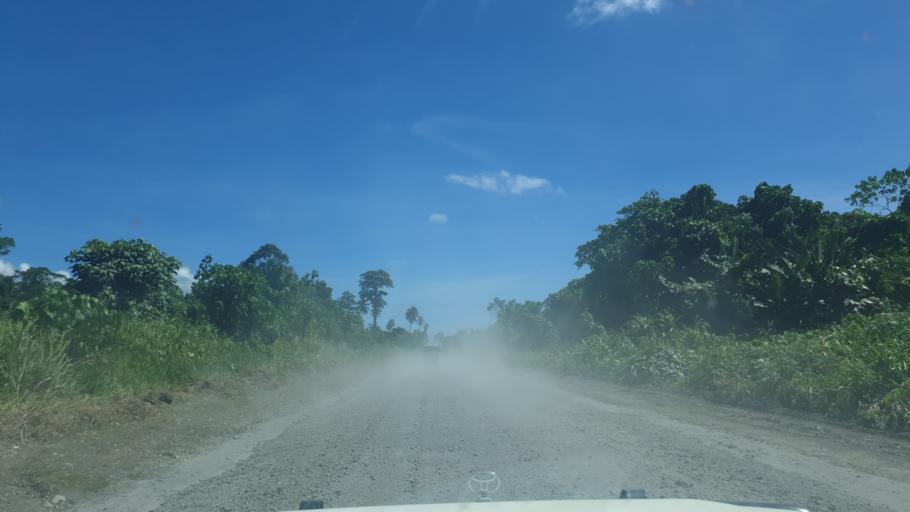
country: PG
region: Bougainville
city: Arawa
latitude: -5.9847
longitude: 155.3563
